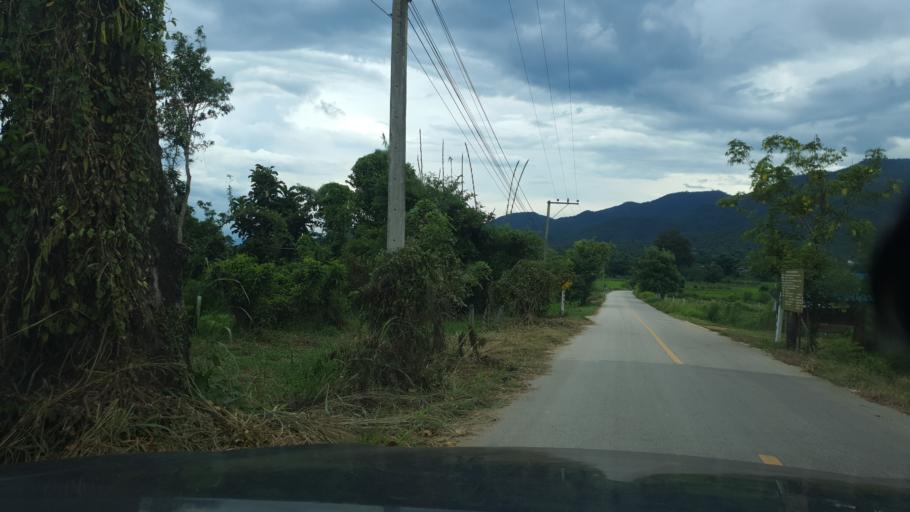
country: TH
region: Lamphun
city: Mae Tha
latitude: 18.5288
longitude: 99.2399
